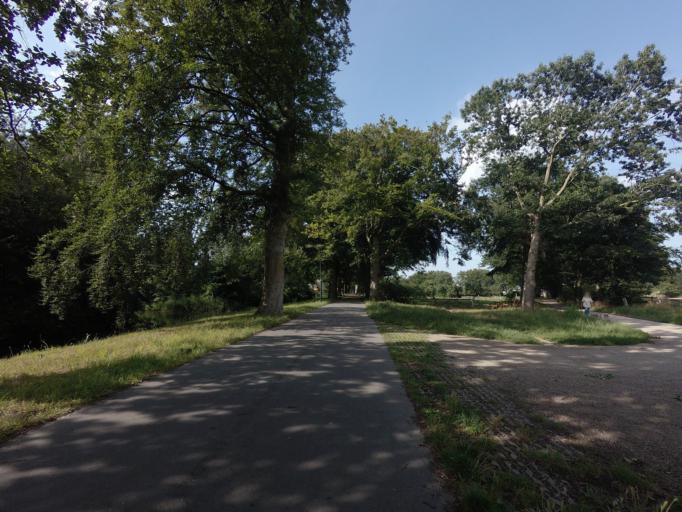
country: NL
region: Overijssel
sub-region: Gemeente Deventer
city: Schalkhaar
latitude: 52.2563
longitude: 6.2122
